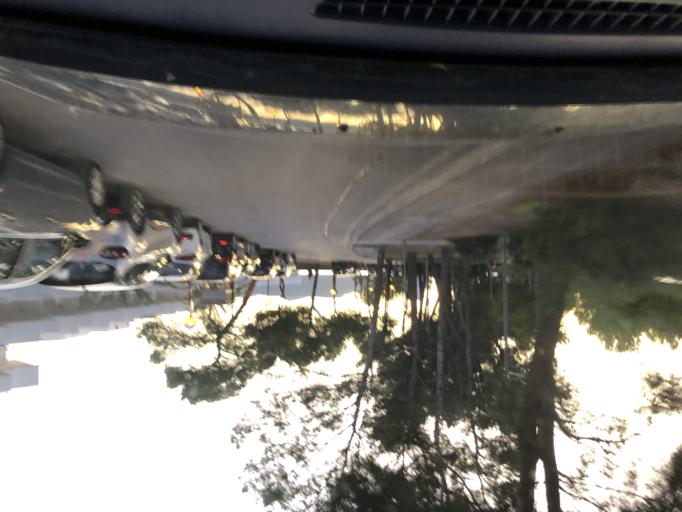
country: ES
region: Balearic Islands
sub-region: Illes Balears
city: Santa Ponsa
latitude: 39.5222
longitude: 2.4709
